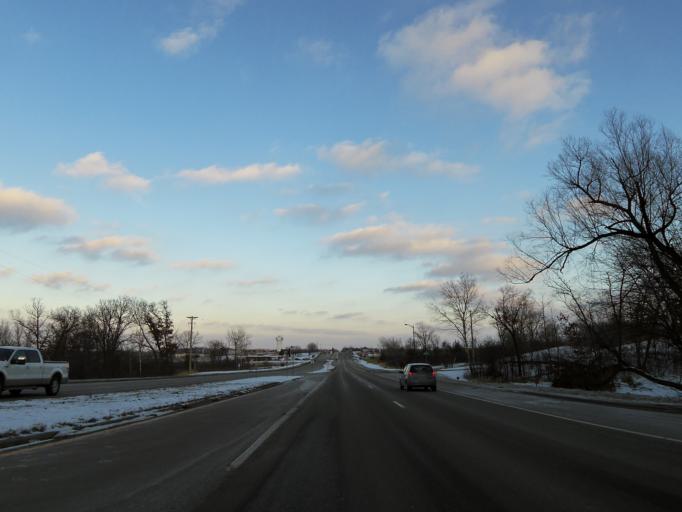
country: US
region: Minnesota
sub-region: Dakota County
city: Lakeville
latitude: 44.6452
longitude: -93.3048
